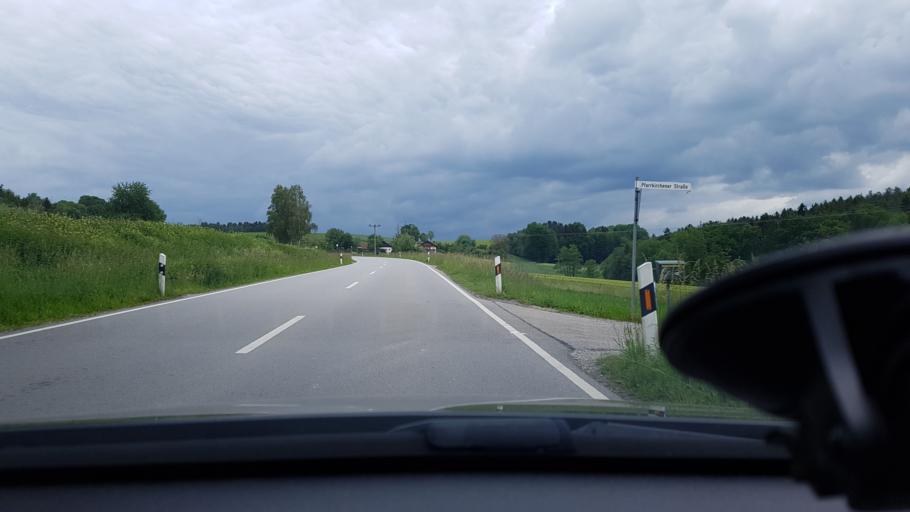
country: DE
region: Bavaria
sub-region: Lower Bavaria
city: Triftern
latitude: 48.3990
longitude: 12.9927
